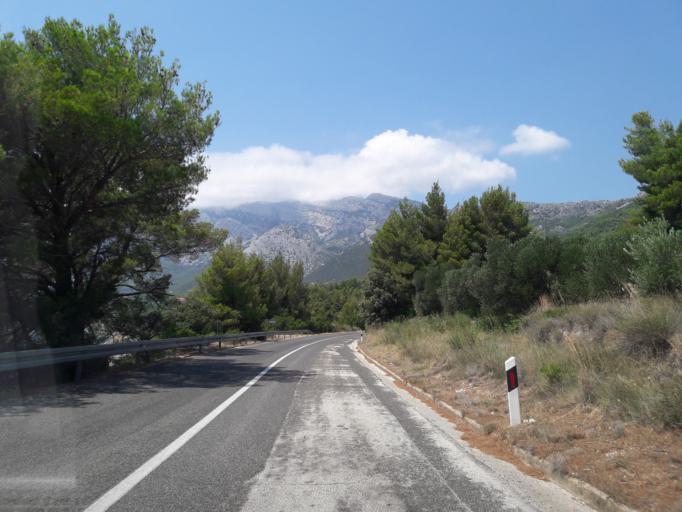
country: HR
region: Dubrovacko-Neretvanska
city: Orebic
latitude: 42.9813
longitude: 17.2189
